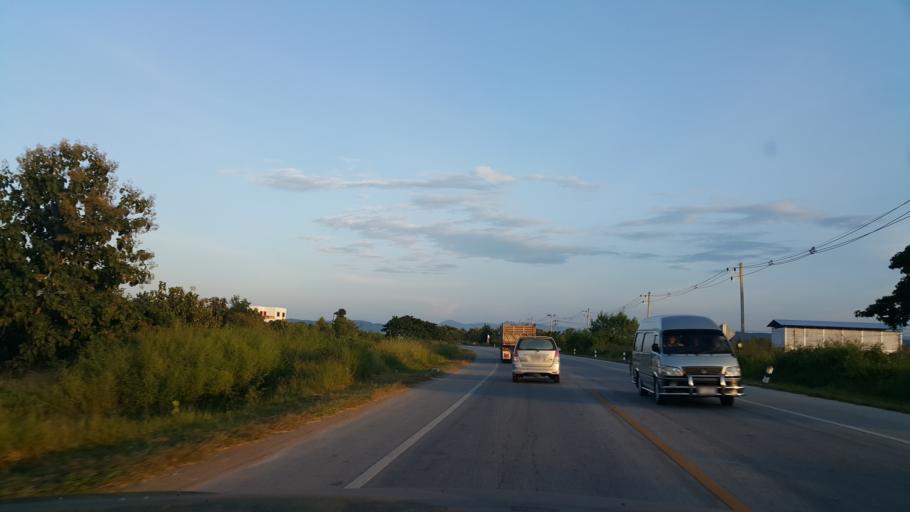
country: TH
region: Lamphun
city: Pa Sang
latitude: 18.4927
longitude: 98.8963
